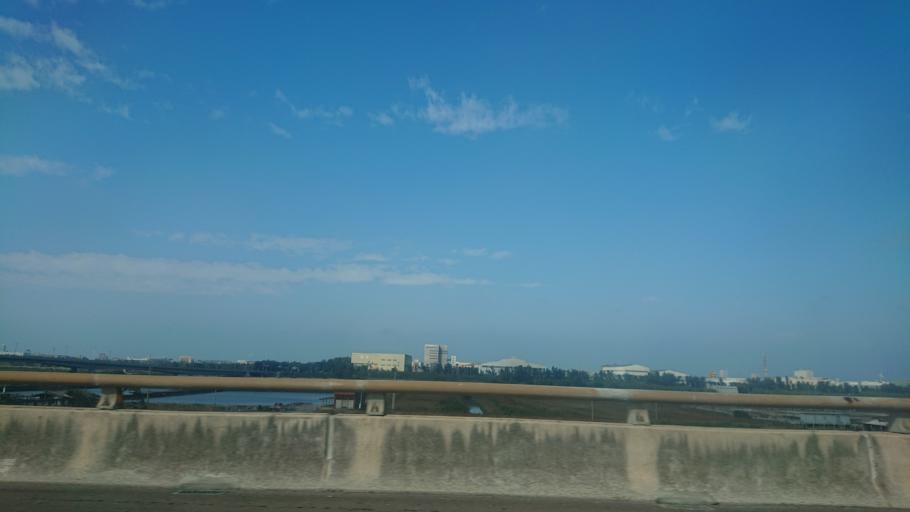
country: TW
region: Taiwan
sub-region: Changhua
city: Chang-hua
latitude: 24.0643
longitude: 120.4114
